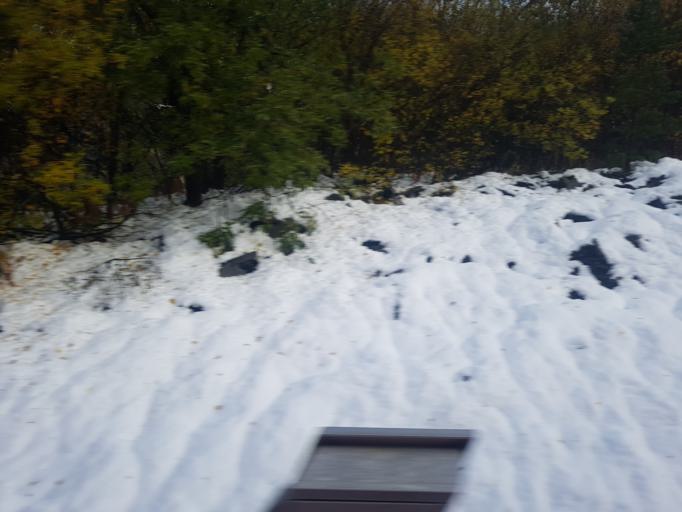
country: NO
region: Sor-Trondelag
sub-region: Oppdal
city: Oppdal
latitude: 62.4354
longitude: 9.6056
